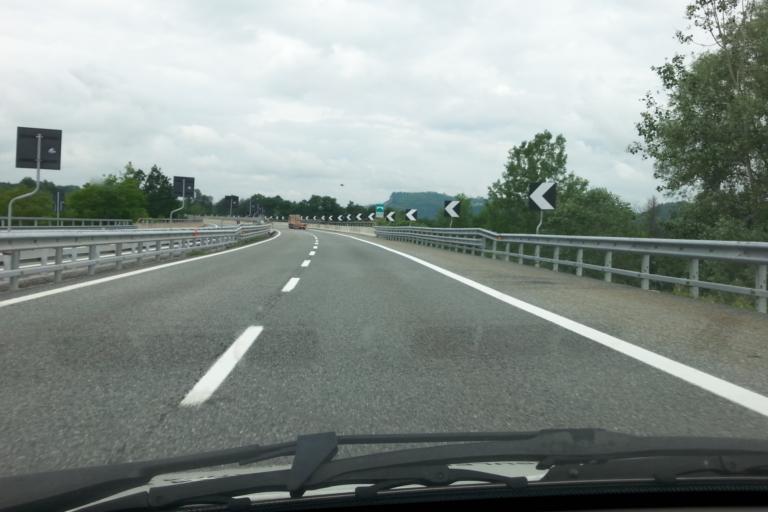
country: IT
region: Piedmont
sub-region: Provincia di Cuneo
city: Lesegno
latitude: 44.4102
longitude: 7.9655
